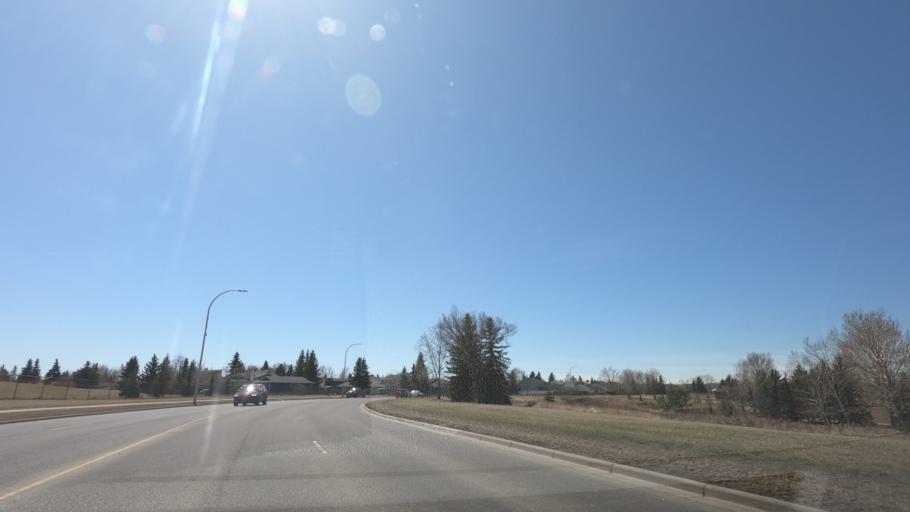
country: CA
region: Alberta
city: Airdrie
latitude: 51.2792
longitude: -114.0087
